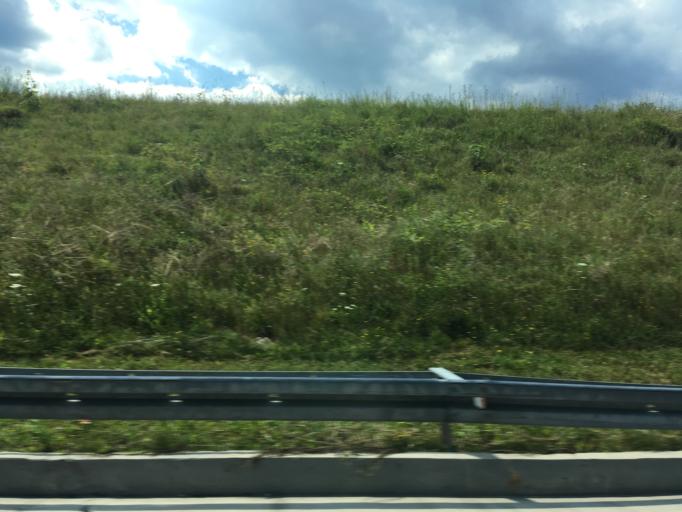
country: HR
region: Karlovacka
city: Ostarije
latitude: 45.1918
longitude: 15.2672
